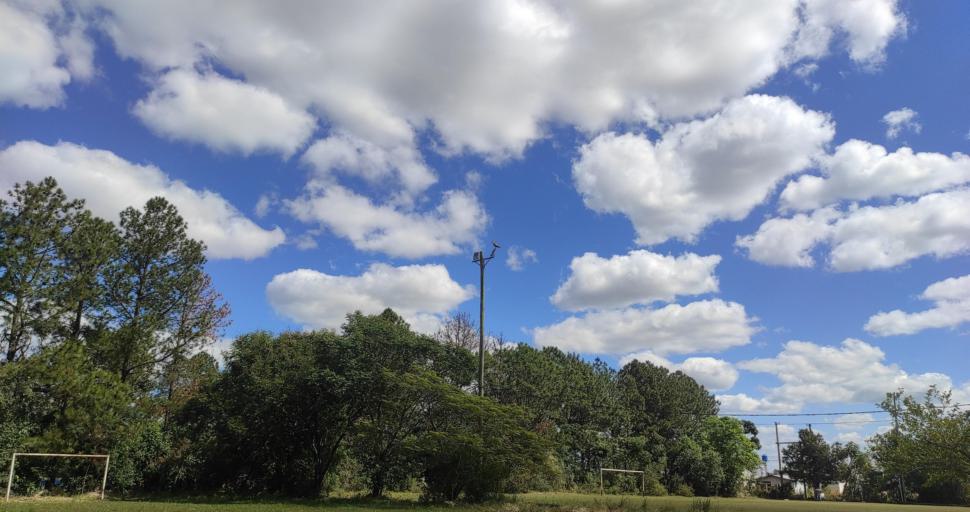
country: AR
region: Misiones
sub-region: Departamento de Capital
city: Posadas
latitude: -27.4007
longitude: -55.9743
